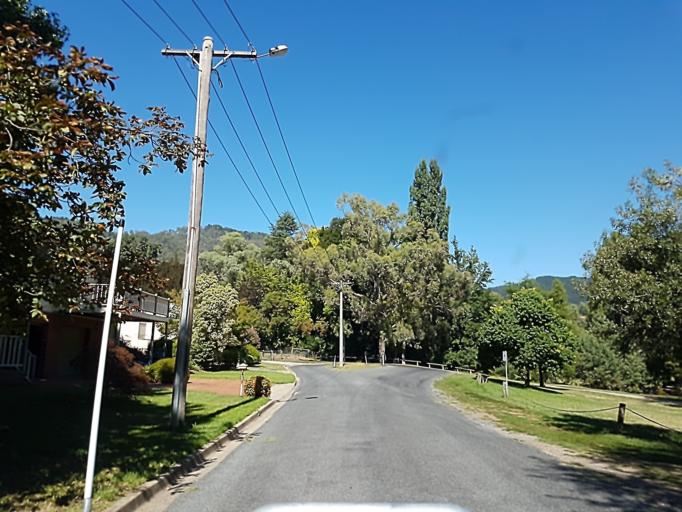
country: AU
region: Victoria
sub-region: Alpine
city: Mount Beauty
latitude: -36.7270
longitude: 146.9578
